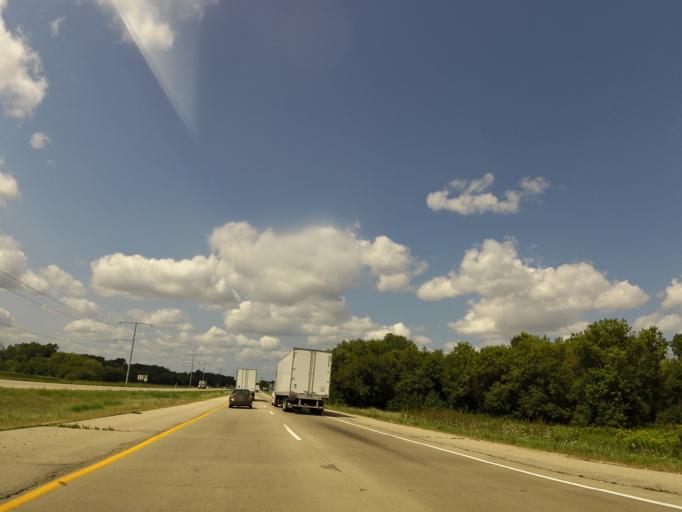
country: US
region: Wisconsin
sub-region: Dane County
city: McFarland
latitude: 43.0363
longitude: -89.2686
